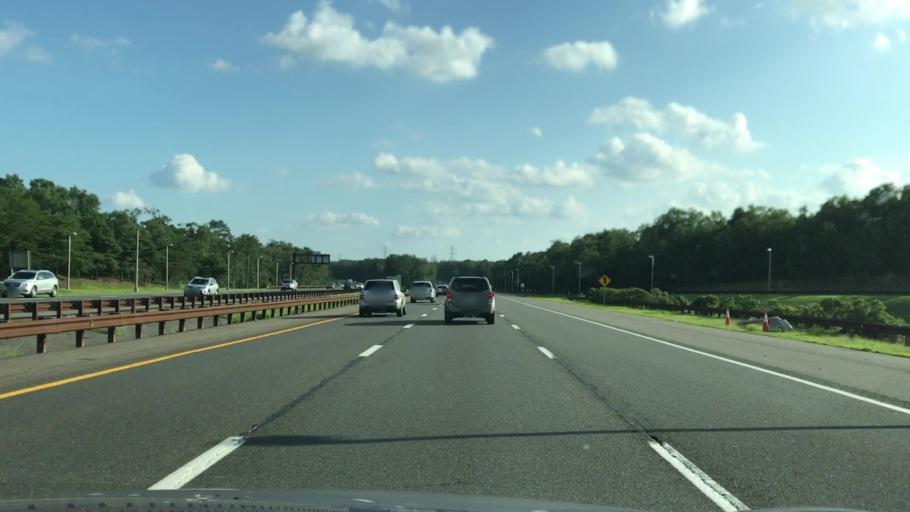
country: US
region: New Jersey
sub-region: Ocean County
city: Forked River
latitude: 39.8619
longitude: -74.2207
